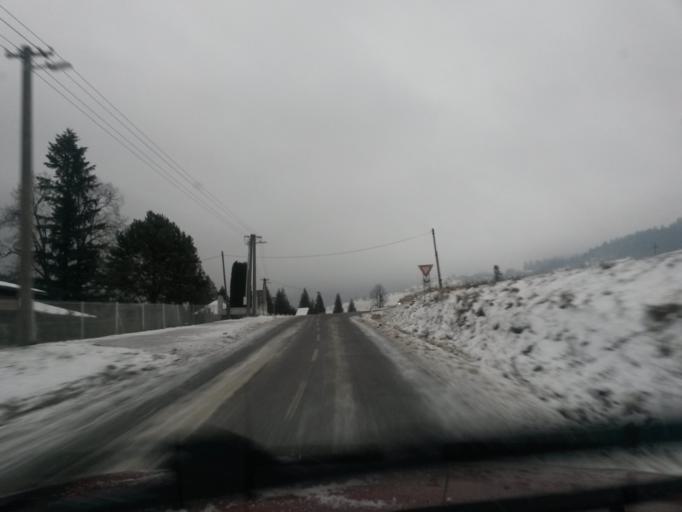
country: SK
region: Kosicky
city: Medzev
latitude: 48.7280
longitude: 20.7258
